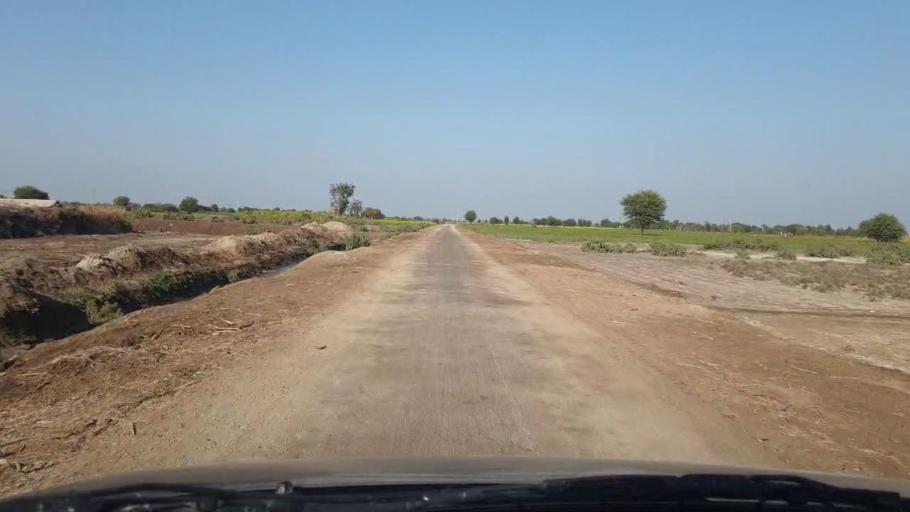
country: PK
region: Sindh
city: Digri
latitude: 25.1431
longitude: 69.2826
